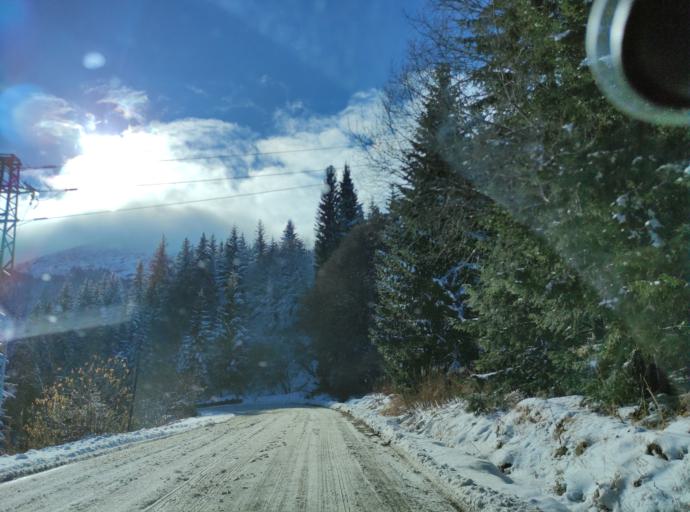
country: BG
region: Sofia-Capital
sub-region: Stolichna Obshtina
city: Sofia
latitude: 42.5884
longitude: 23.2968
